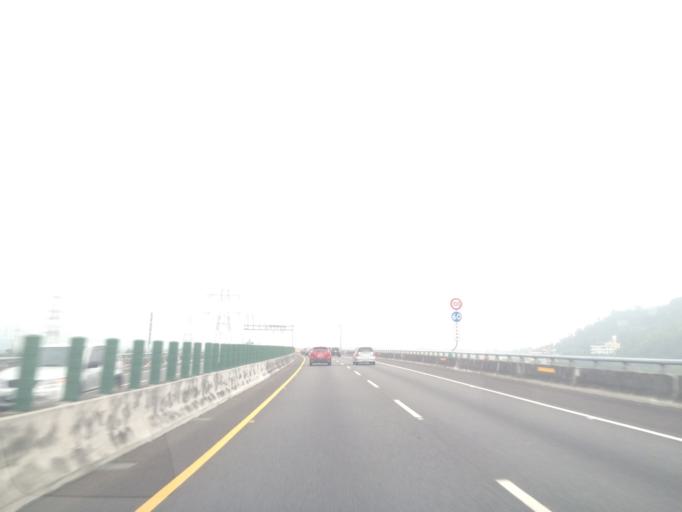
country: TW
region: Taiwan
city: Zhongxing New Village
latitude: 24.0081
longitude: 120.7066
